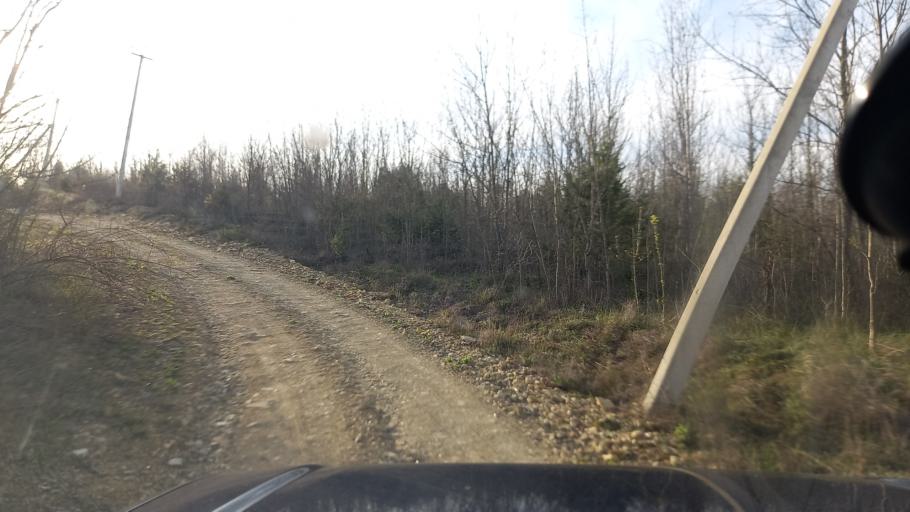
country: RU
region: Krasnodarskiy
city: Arkhipo-Osipovka
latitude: 44.3622
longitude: 38.5654
